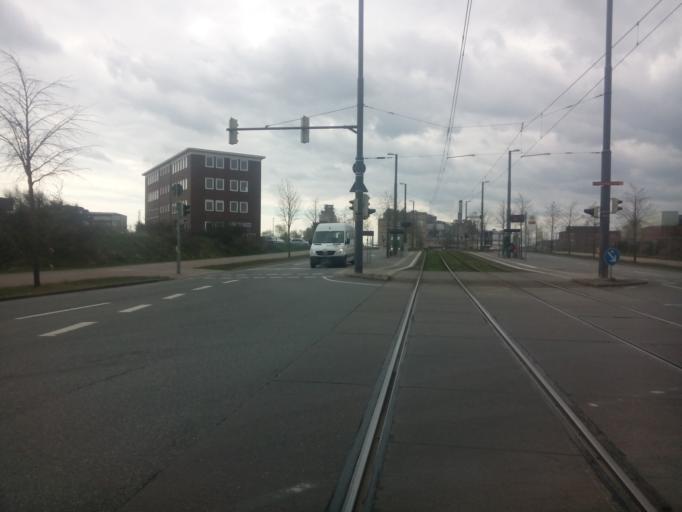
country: DE
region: Bremen
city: Bremen
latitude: 53.0870
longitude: 8.7827
